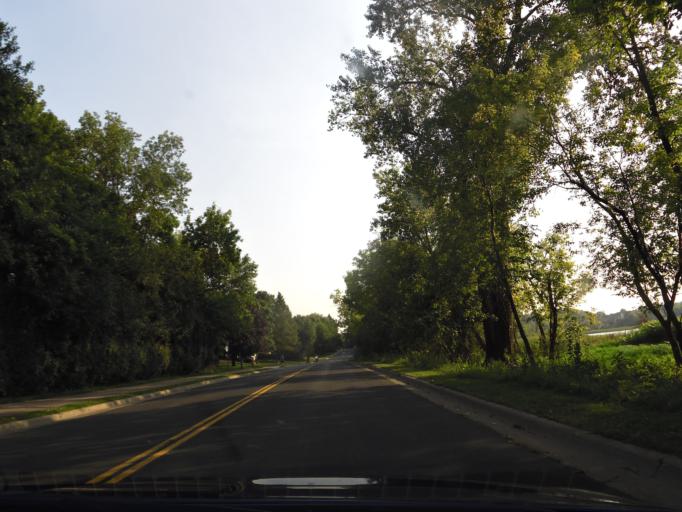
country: US
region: Minnesota
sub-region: Hennepin County
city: Shorewood
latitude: 44.8766
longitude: -93.6201
